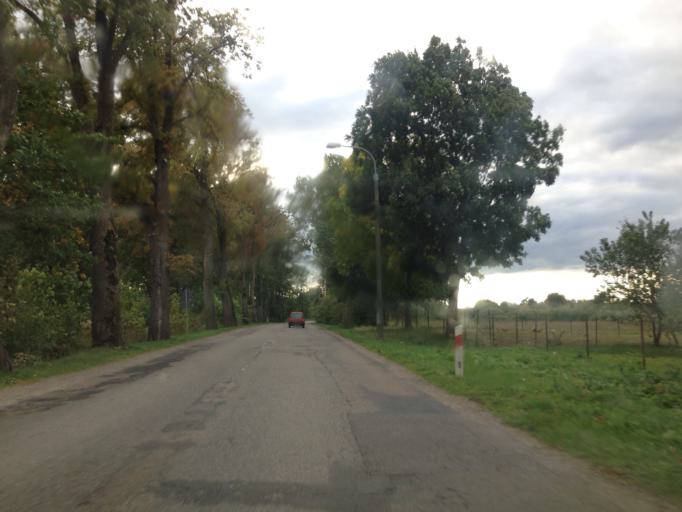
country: PL
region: Pomeranian Voivodeship
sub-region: Powiat kwidzynski
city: Prabuty
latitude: 53.7527
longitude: 19.1905
